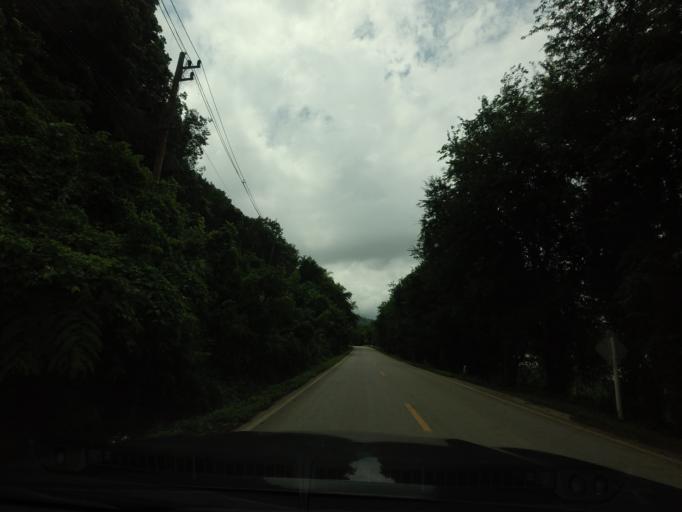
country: TH
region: Loei
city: Pak Chom
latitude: 18.0541
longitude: 101.8111
